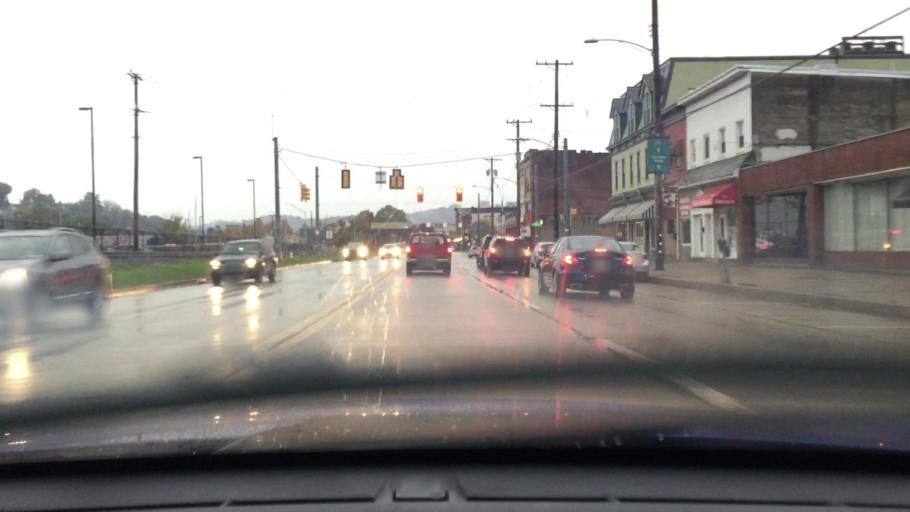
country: US
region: Pennsylvania
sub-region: Allegheny County
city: Carnegie
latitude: 40.4041
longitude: -80.0919
